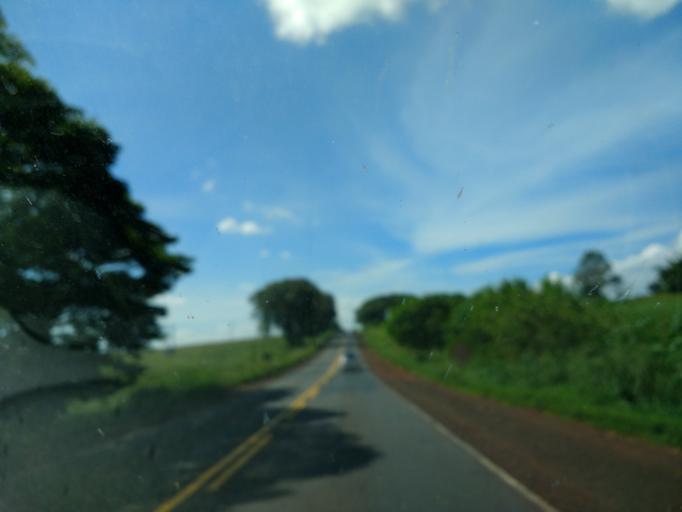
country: BR
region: Parana
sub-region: Paicandu
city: Paicandu
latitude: -23.5645
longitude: -52.2503
